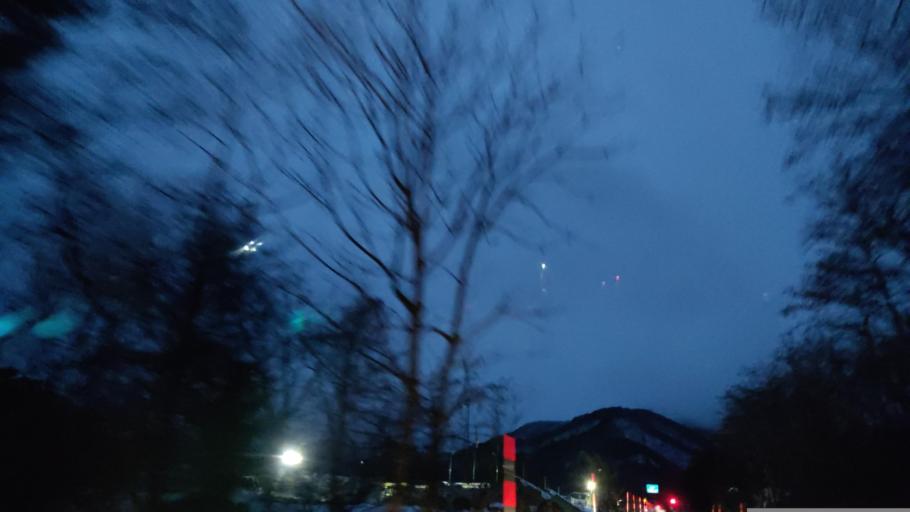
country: JP
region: Iwate
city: Morioka-shi
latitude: 39.6342
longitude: 141.0955
